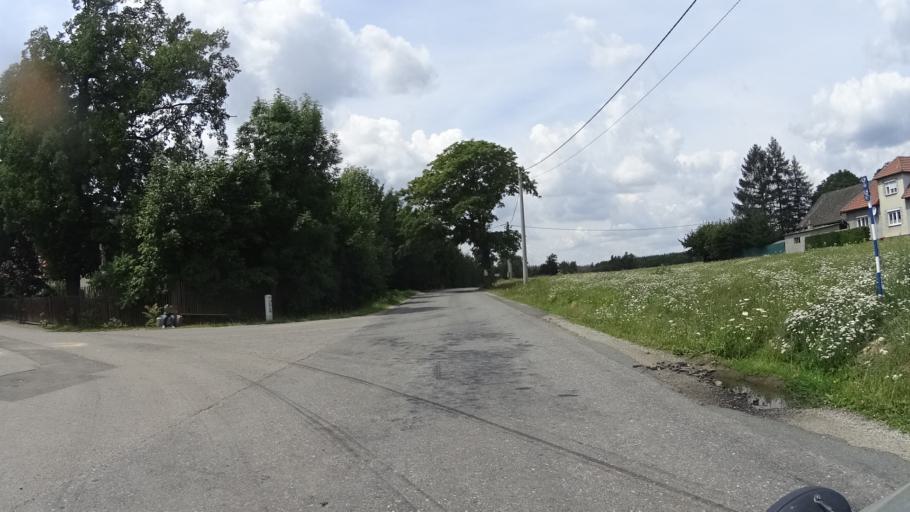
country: CZ
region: Vysocina
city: Merin
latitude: 49.4115
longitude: 15.9457
